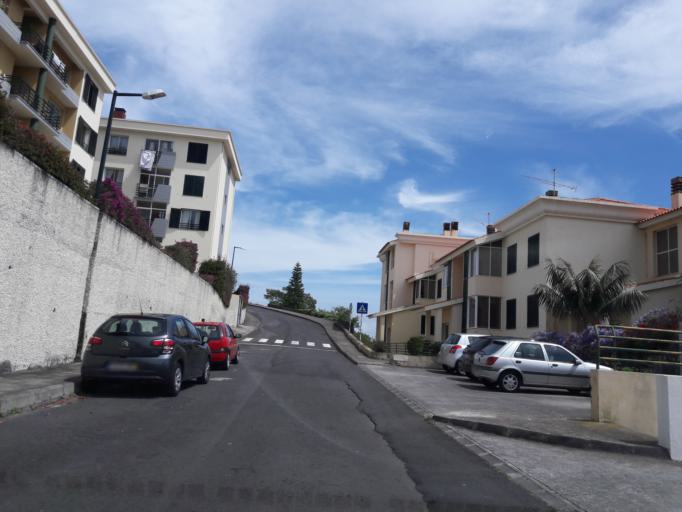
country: PT
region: Madeira
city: Canico
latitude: 32.6521
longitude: -16.8526
